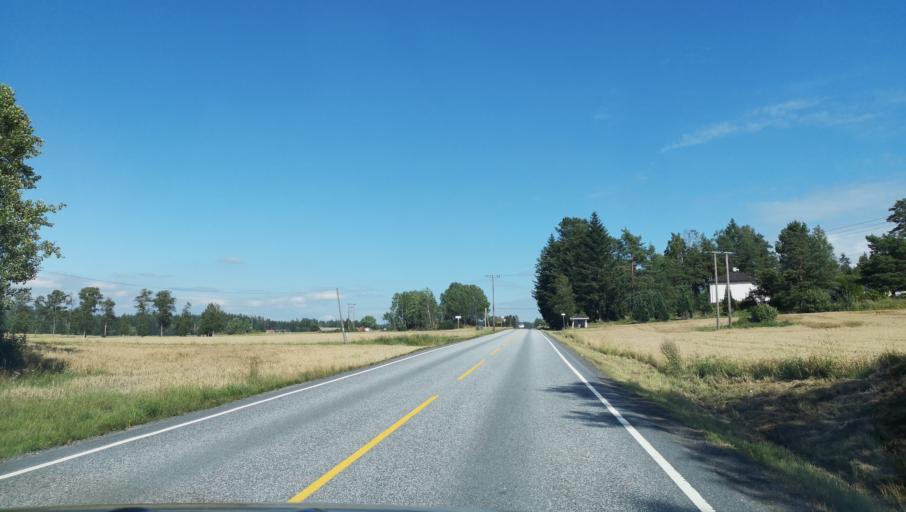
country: NO
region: Akershus
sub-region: Vestby
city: Vestby
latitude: 59.5450
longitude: 10.7905
